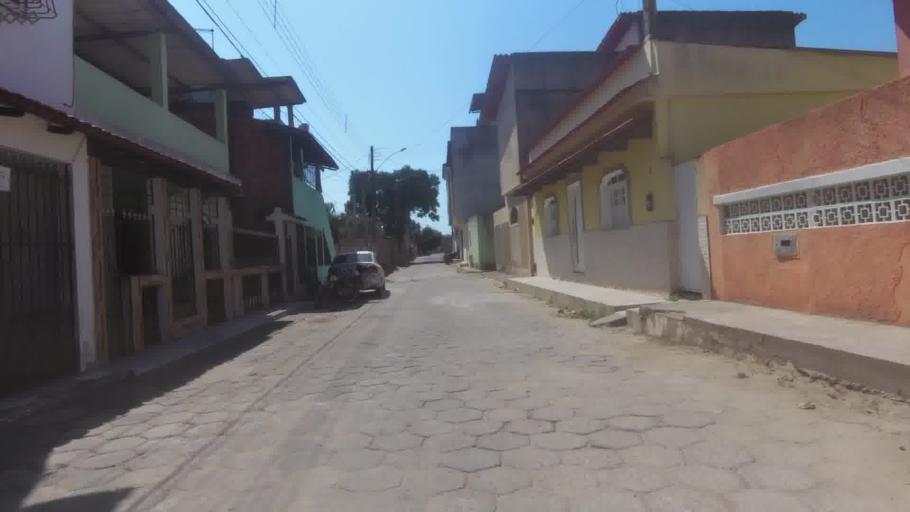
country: BR
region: Espirito Santo
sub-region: Itapemirim
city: Itapemirim
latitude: -21.0077
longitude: -40.8123
